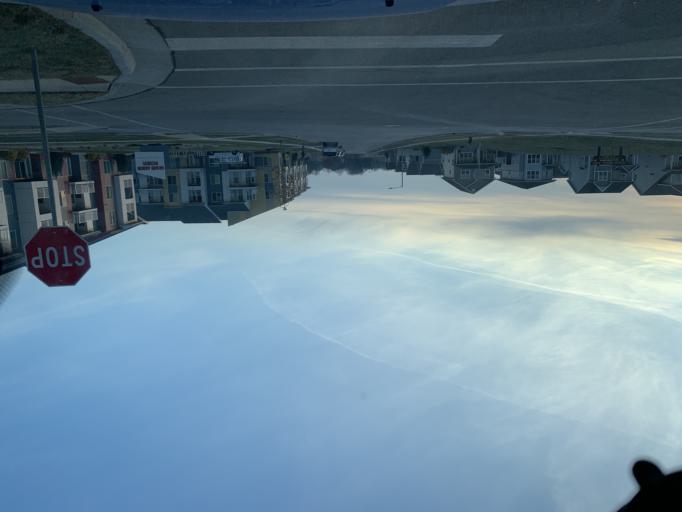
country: US
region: Wisconsin
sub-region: Dane County
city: Middleton
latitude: 43.0589
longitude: -89.5631
